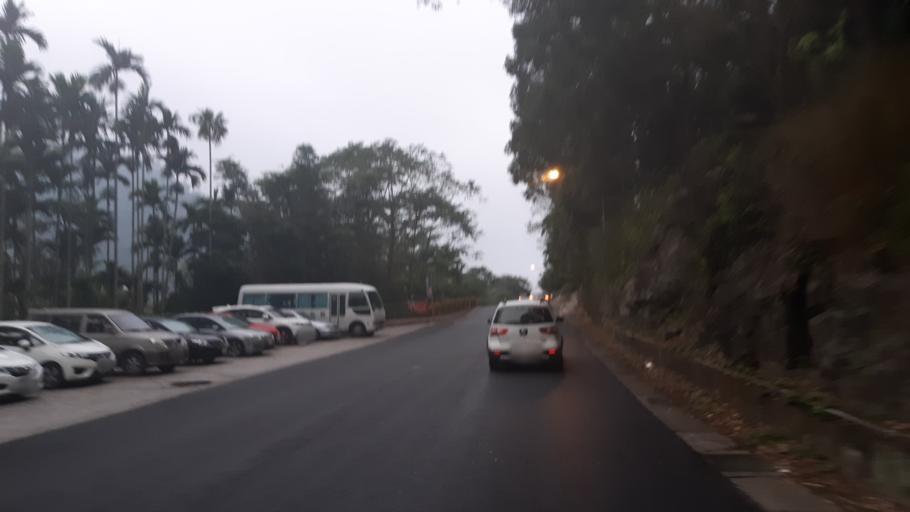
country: TW
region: Taiwan
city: Daxi
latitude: 24.7019
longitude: 121.1865
